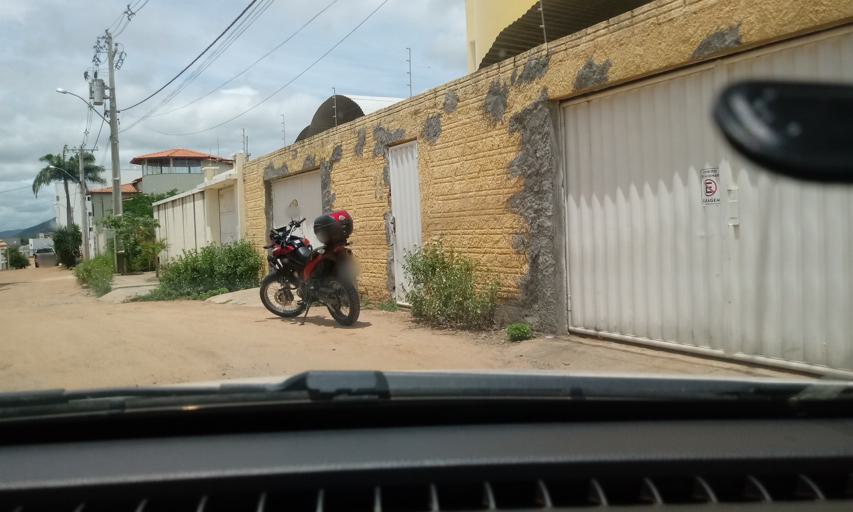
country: BR
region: Bahia
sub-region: Guanambi
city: Guanambi
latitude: -14.2299
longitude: -42.7768
